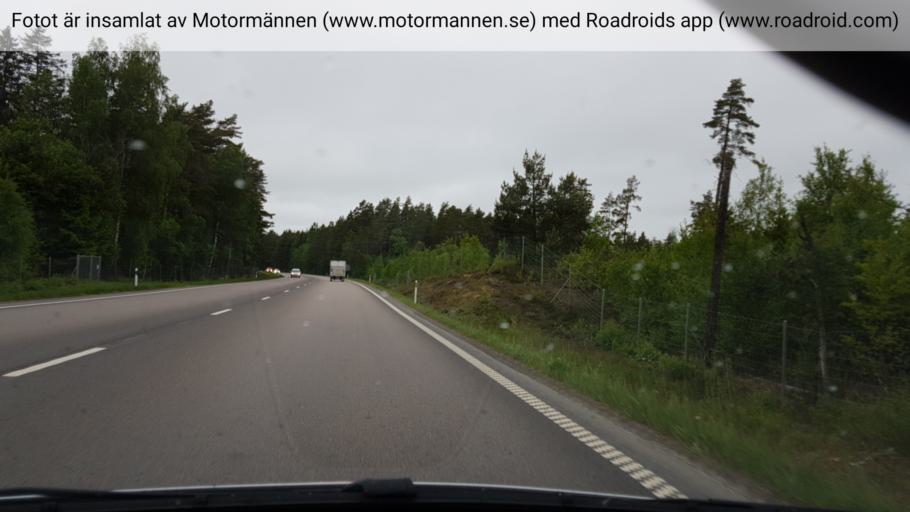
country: SE
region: Vaestra Goetaland
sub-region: Skara Kommun
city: Skara
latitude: 58.4160
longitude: 13.3656
